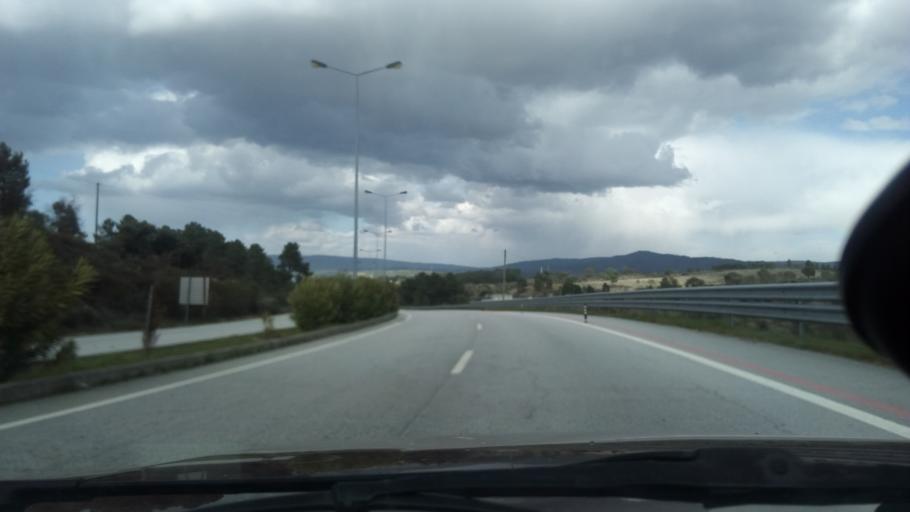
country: PT
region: Guarda
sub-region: Celorico da Beira
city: Celorico da Beira
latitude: 40.6307
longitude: -7.3873
